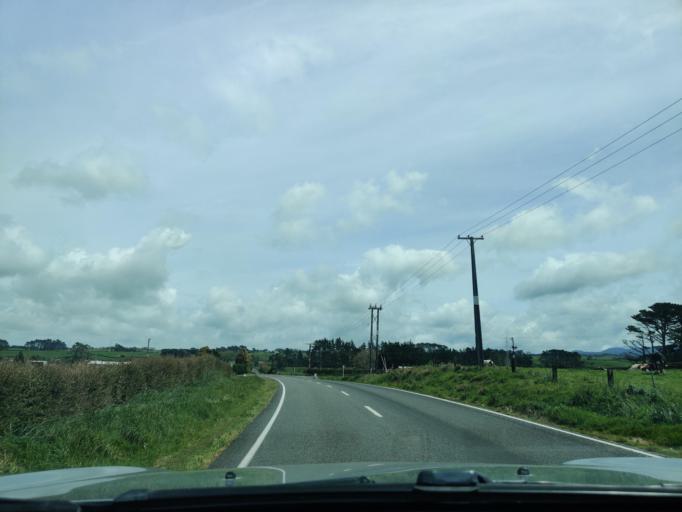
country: NZ
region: Taranaki
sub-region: South Taranaki District
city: Eltham
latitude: -39.3714
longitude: 174.1952
